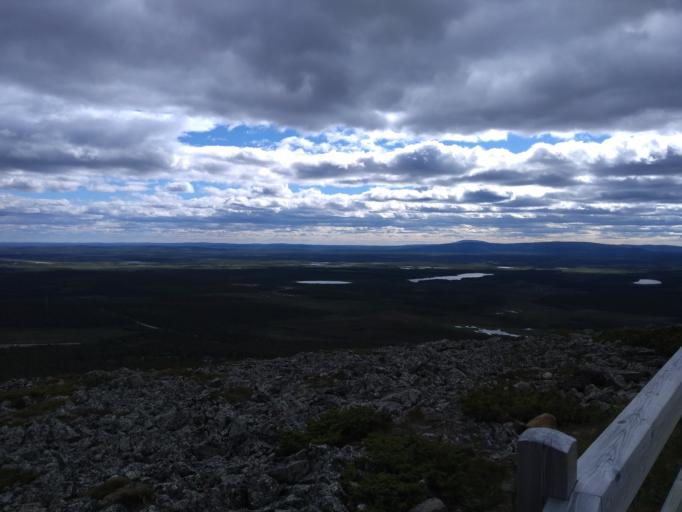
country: FI
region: Lapland
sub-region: Tunturi-Lappi
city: Kittilae
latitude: 67.7833
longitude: 24.8581
